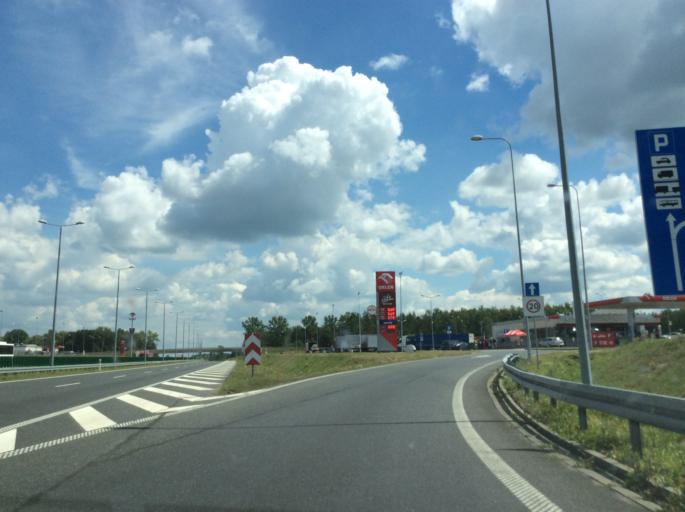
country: PL
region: Lodz Voivodeship
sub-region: Powiat zgierski
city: Parzeczew
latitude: 51.9454
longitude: 19.1750
